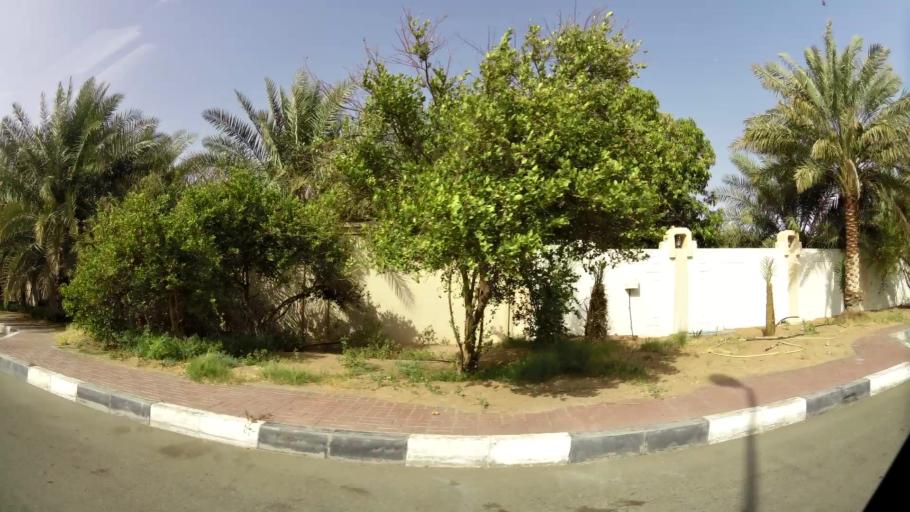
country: AE
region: Abu Dhabi
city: Al Ain
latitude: 24.2299
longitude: 55.6615
